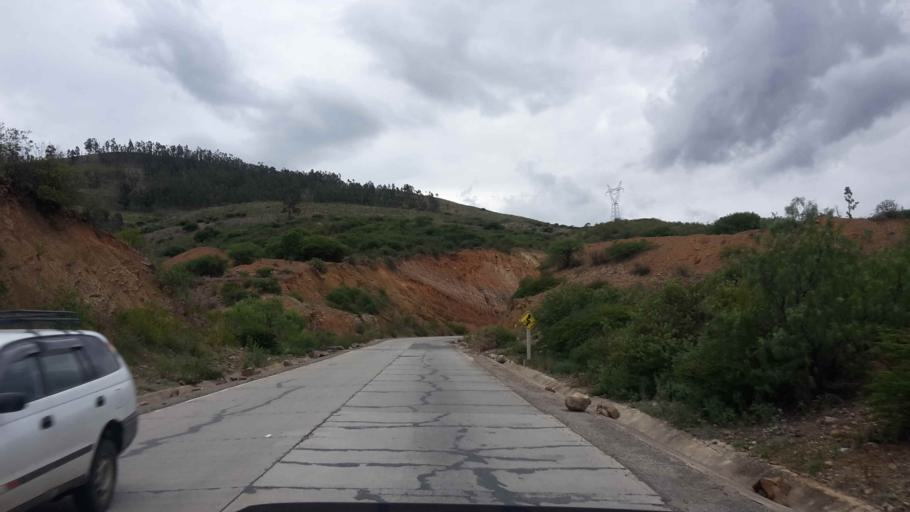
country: BO
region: Cochabamba
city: Cochabamba
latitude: -17.5319
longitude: -66.2014
